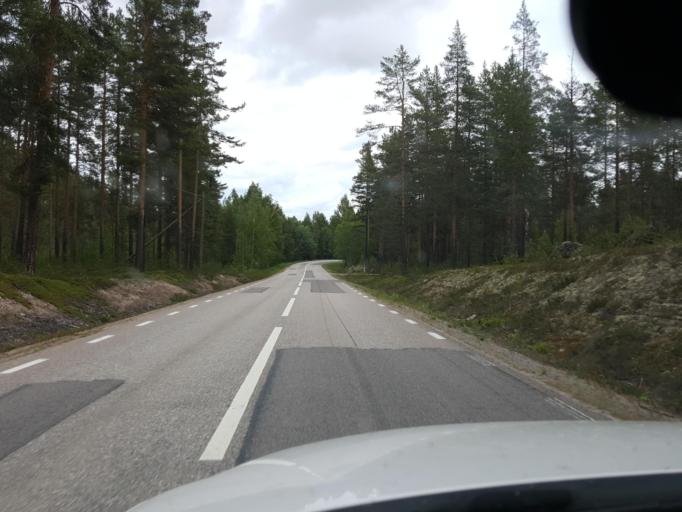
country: SE
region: Gaevleborg
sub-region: Ljusdals Kommun
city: Farila
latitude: 61.7853
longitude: 15.6144
